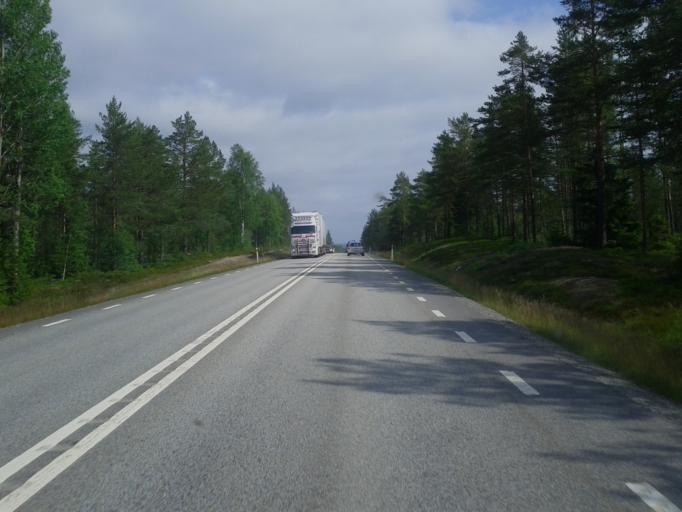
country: SE
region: Vaesterbotten
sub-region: Robertsfors Kommun
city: Robertsfors
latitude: 64.1943
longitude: 21.0042
